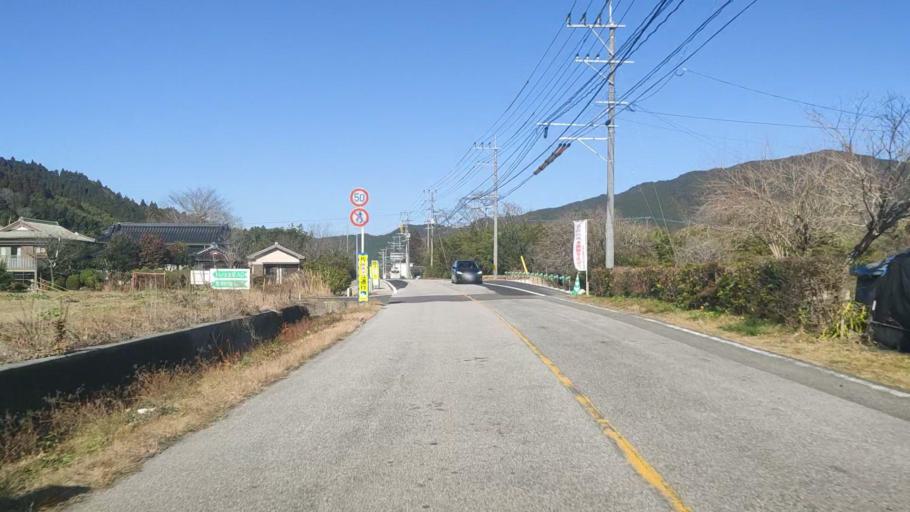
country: JP
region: Oita
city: Saiki
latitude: 32.9175
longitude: 131.9281
